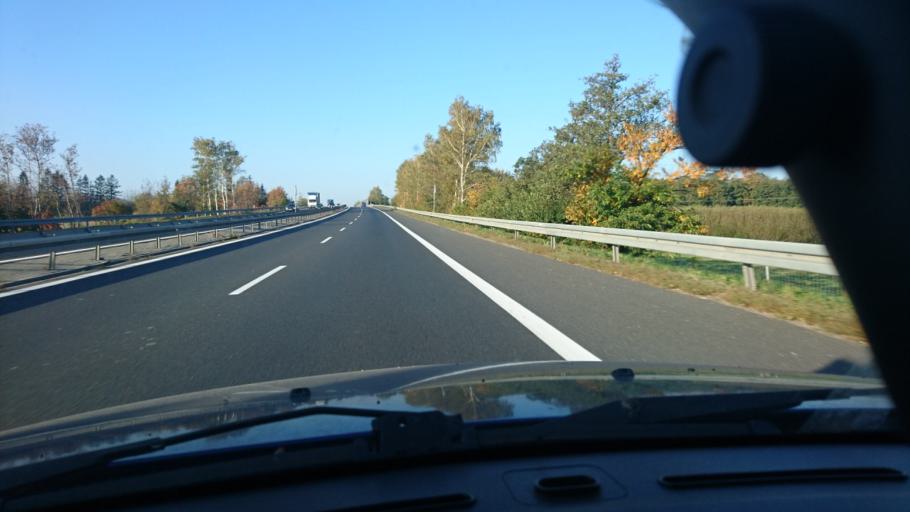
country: PL
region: Silesian Voivodeship
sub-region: Powiat bielski
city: Jasienica
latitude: 49.8091
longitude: 18.9080
